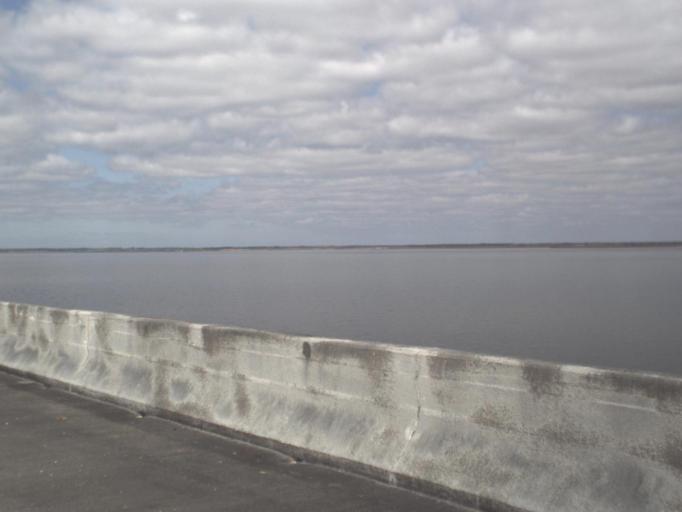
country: US
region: Florida
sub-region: Franklin County
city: Eastpoint
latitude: 29.7314
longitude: -84.9308
